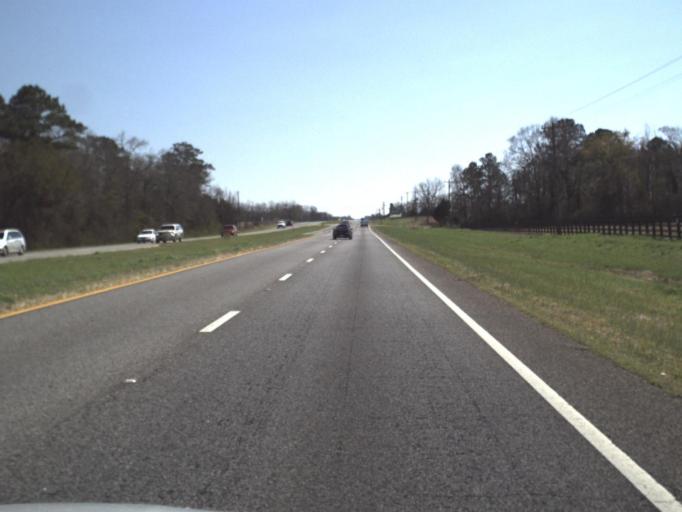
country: US
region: Florida
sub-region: Jackson County
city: Graceville
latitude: 30.9335
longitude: -85.3887
